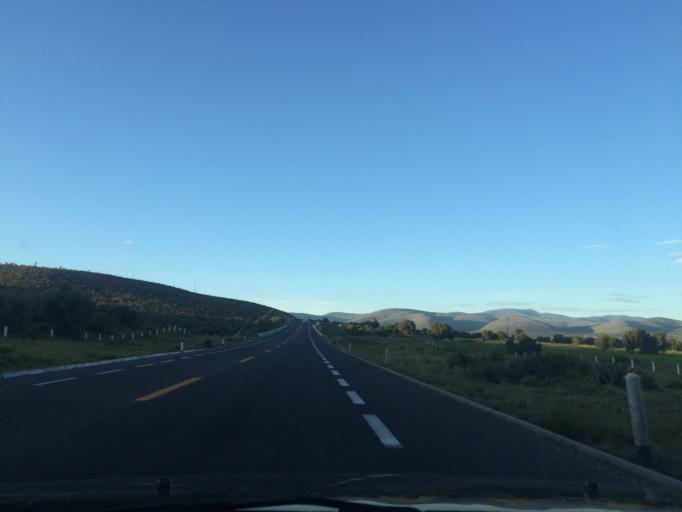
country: MX
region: Puebla
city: Cuacnopalan
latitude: 18.7933
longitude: -97.4892
